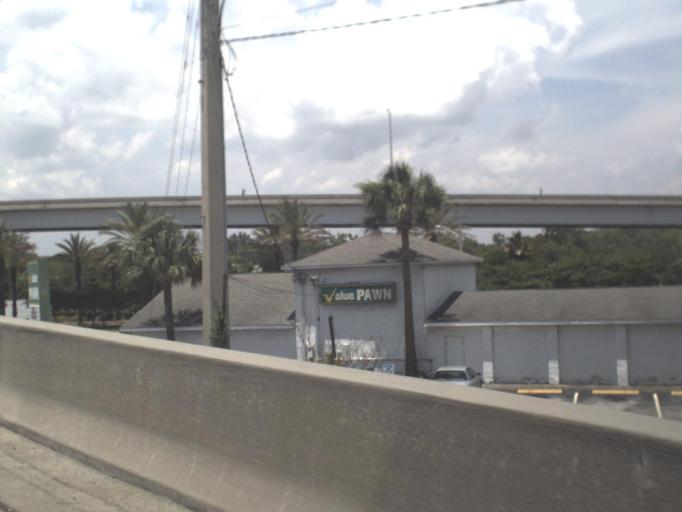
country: US
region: Florida
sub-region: Duval County
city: Atlantic Beach
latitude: 30.3244
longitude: -81.4186
